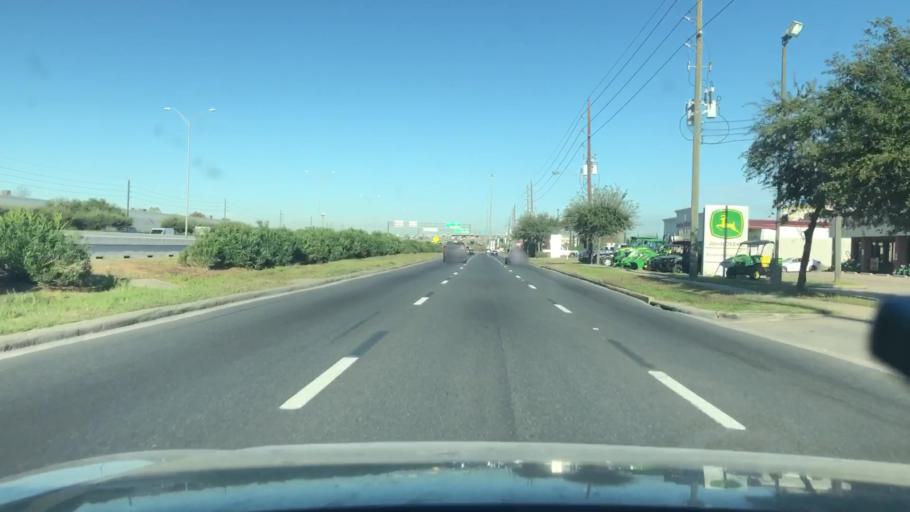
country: US
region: Texas
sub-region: Fort Bend County
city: Missouri City
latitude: 29.6497
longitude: -95.5451
